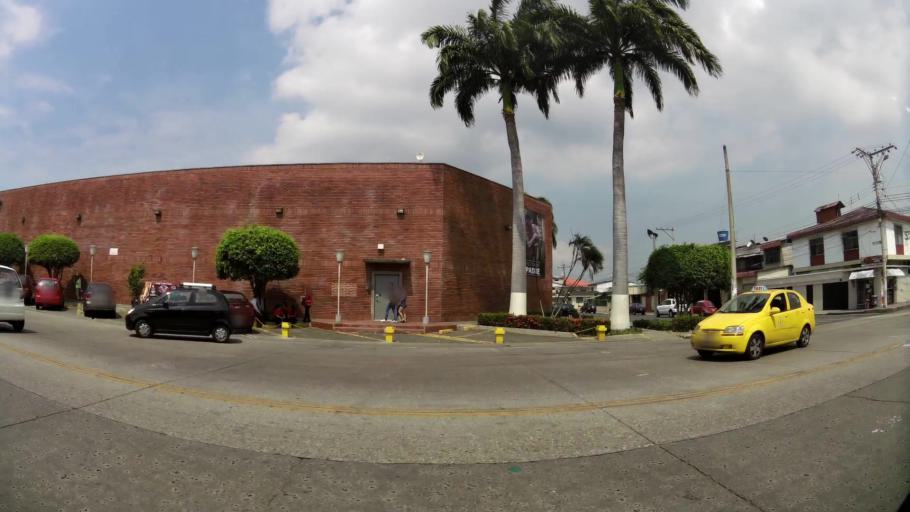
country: EC
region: Guayas
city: Guayaquil
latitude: -2.2306
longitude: -79.8959
